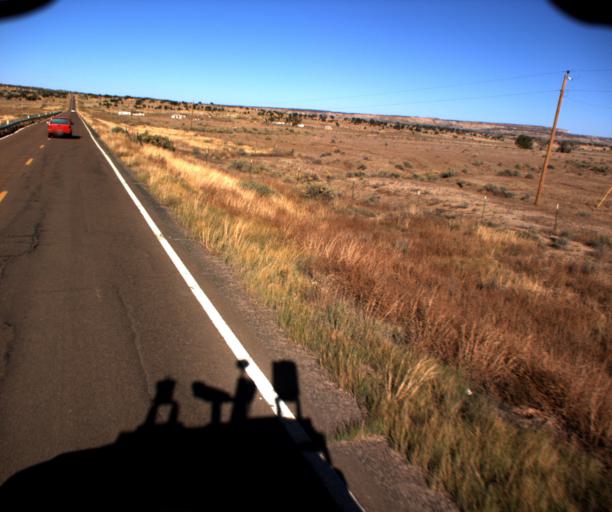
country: US
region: Arizona
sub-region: Apache County
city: Ganado
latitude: 35.7488
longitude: -109.8752
